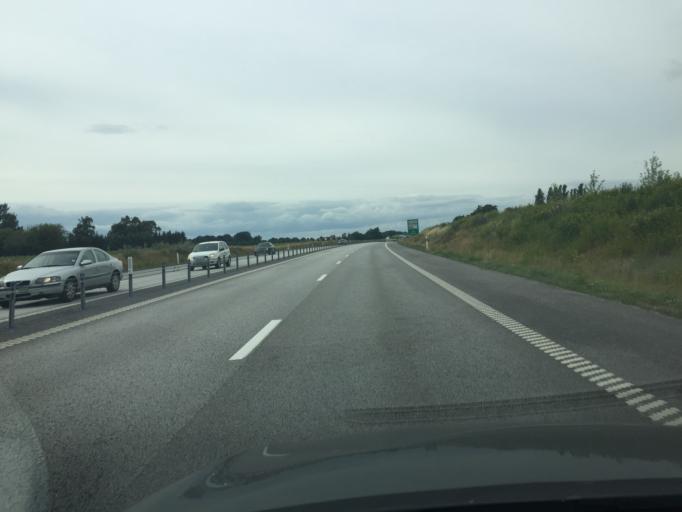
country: SE
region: Skane
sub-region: Trelleborgs Kommun
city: Skare
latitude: 55.4256
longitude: 13.0534
